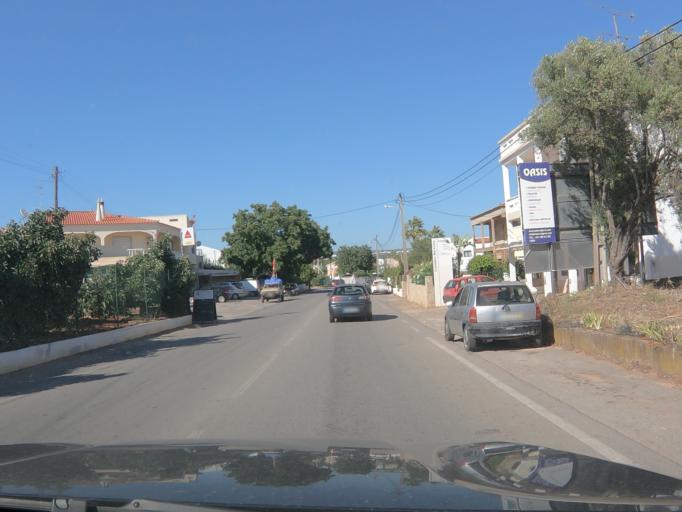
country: PT
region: Faro
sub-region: Loule
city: Almancil
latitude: 37.1014
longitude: -8.0590
